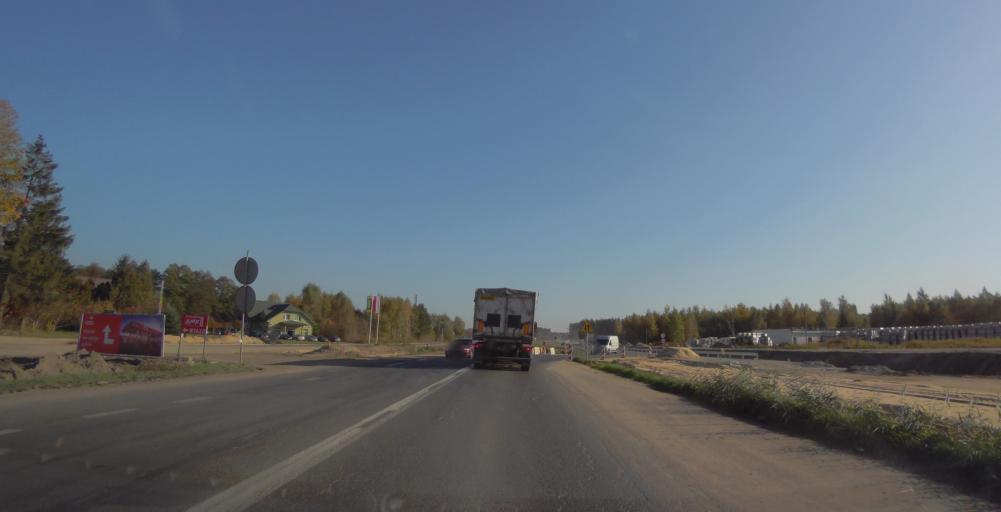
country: PL
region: Masovian Voivodeship
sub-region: Powiat otwocki
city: Celestynow
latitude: 52.1182
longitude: 21.3682
